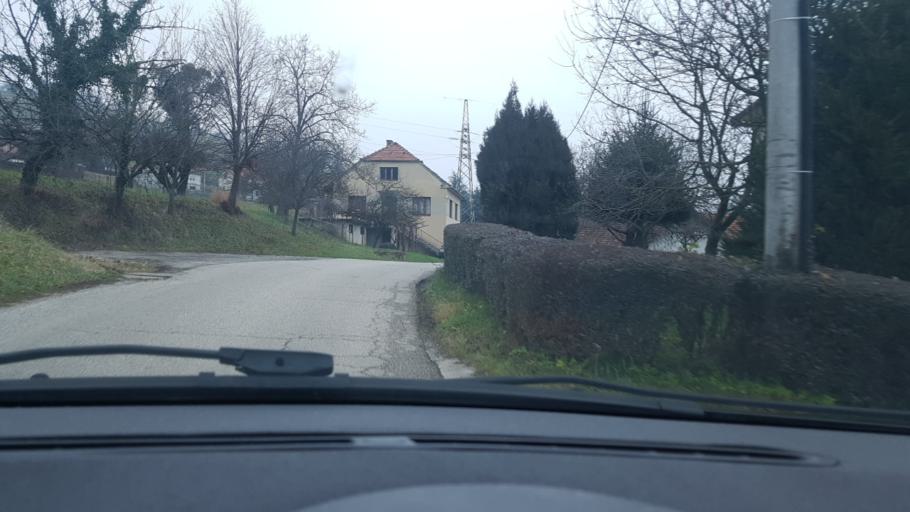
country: HR
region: Krapinsko-Zagorska
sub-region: Grad Krapina
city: Krapina
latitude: 46.1475
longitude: 15.8672
